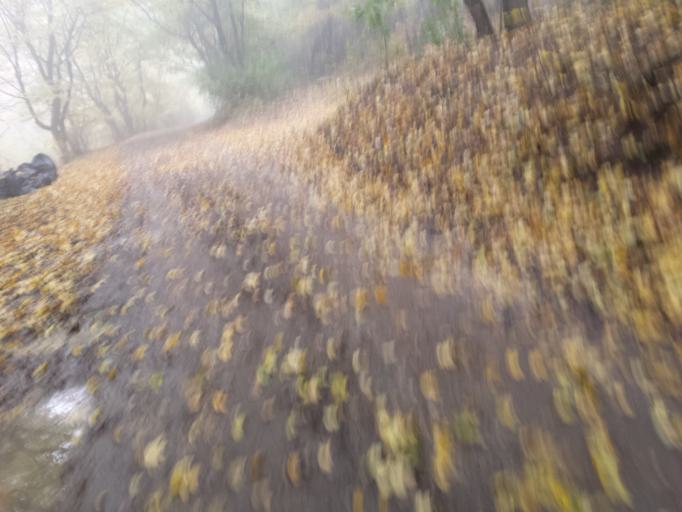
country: RO
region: Cluj
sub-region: Municipiul Cluj-Napoca
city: Cluj-Napoca
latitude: 46.7755
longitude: 23.5554
